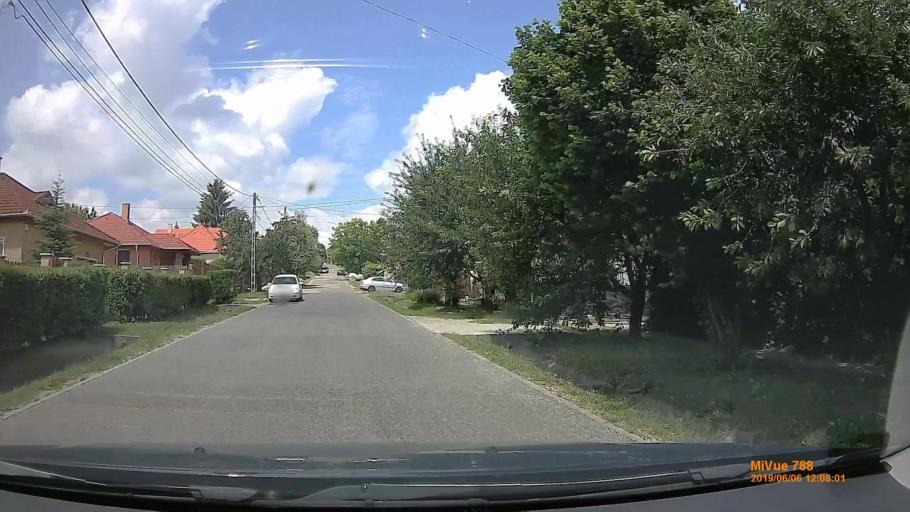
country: HU
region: Pest
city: Kerepes
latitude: 47.5670
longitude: 19.2677
